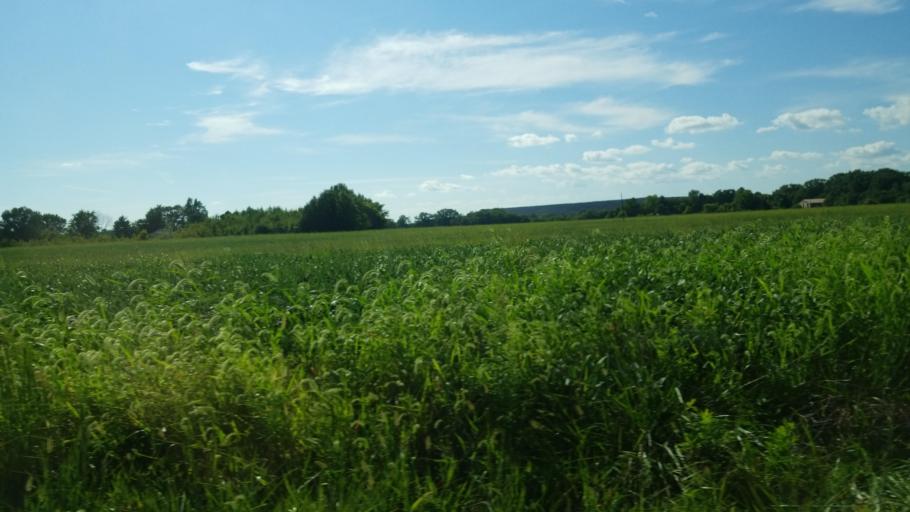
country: US
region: Illinois
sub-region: Saline County
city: Harrisburg
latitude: 37.8139
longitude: -88.5534
